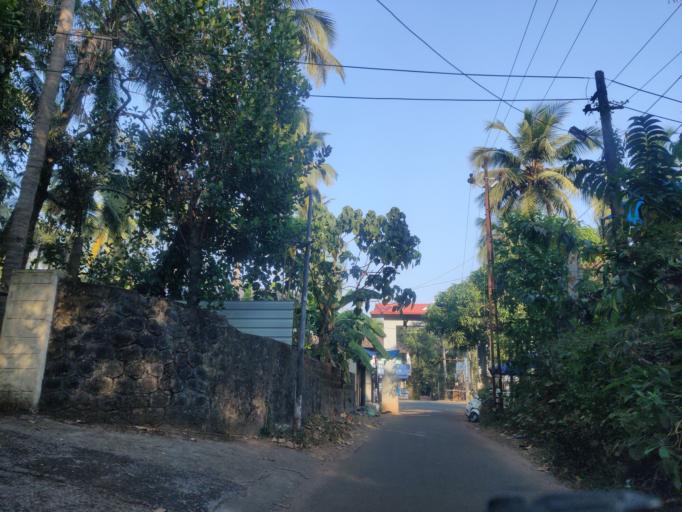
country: IN
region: Kerala
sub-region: Malappuram
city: Ponnani
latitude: 10.7287
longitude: 76.0120
